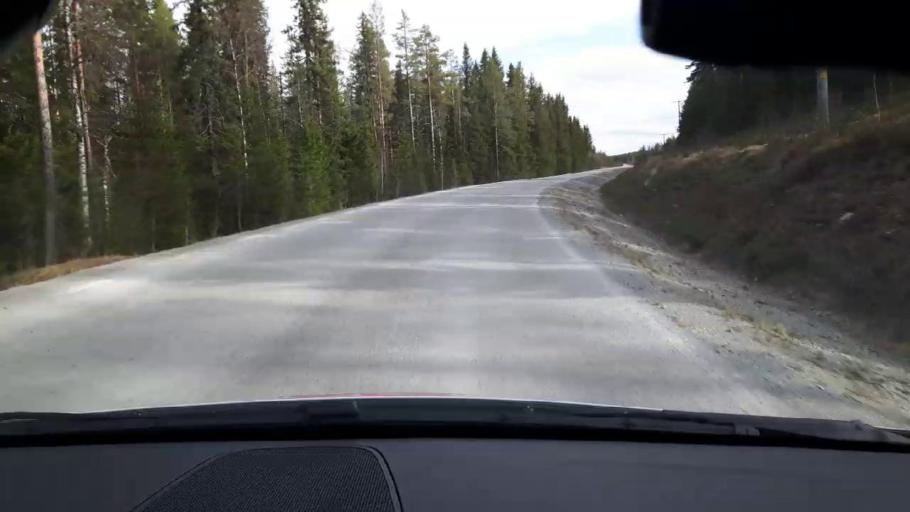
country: SE
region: Jaemtland
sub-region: Bergs Kommun
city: Hoverberg
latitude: 62.7184
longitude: 14.6056
